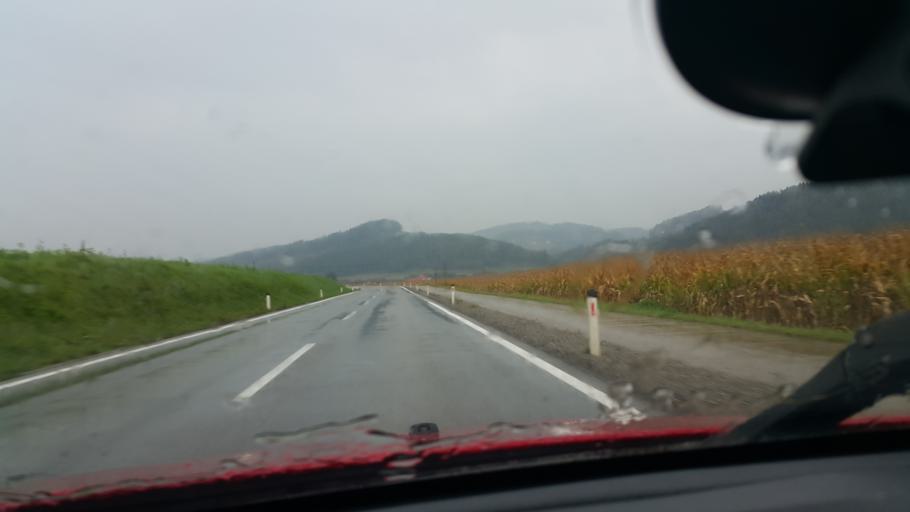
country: AT
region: Carinthia
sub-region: Politischer Bezirk Volkermarkt
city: Ruden
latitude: 46.6678
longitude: 14.7709
